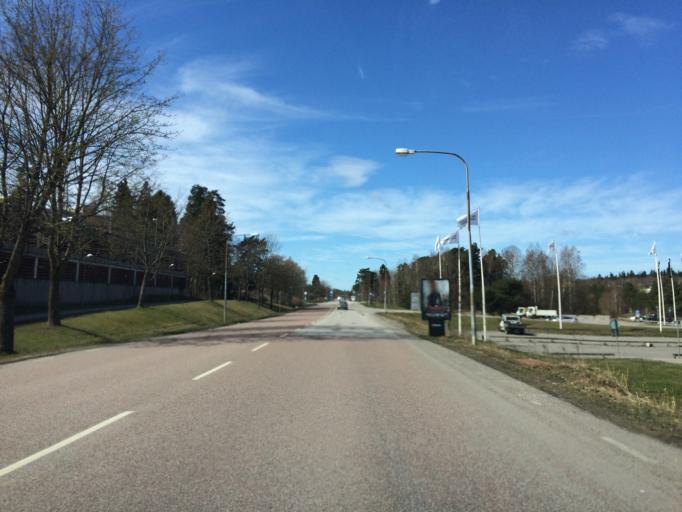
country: SE
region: Stockholm
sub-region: Stockholms Kommun
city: Kista
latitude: 59.4168
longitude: 17.9190
